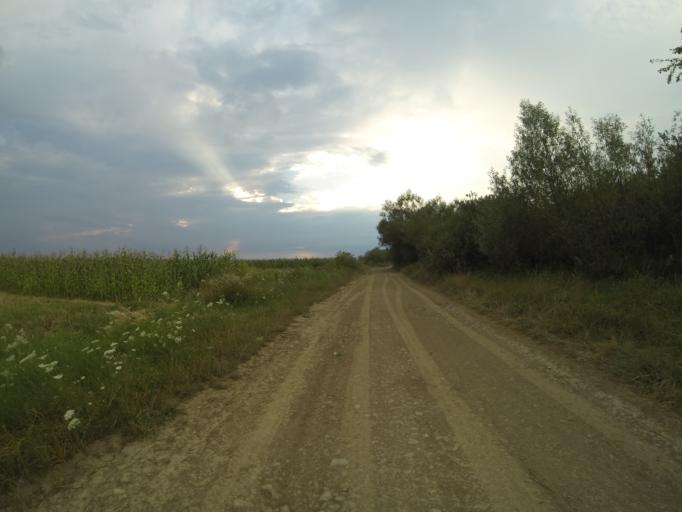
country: RO
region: Brasov
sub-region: Comuna Sinca Veche
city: Sinca Veche
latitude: 45.7726
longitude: 25.1699
